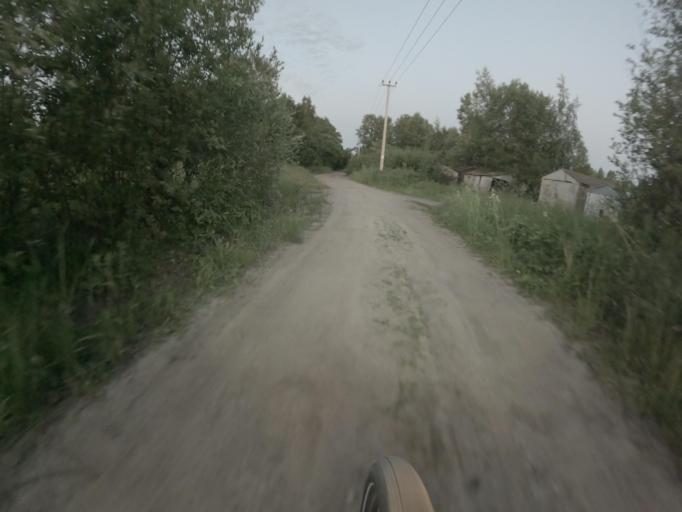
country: RU
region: Leningrad
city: Imeni Sverdlova
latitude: 59.7806
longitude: 30.6896
